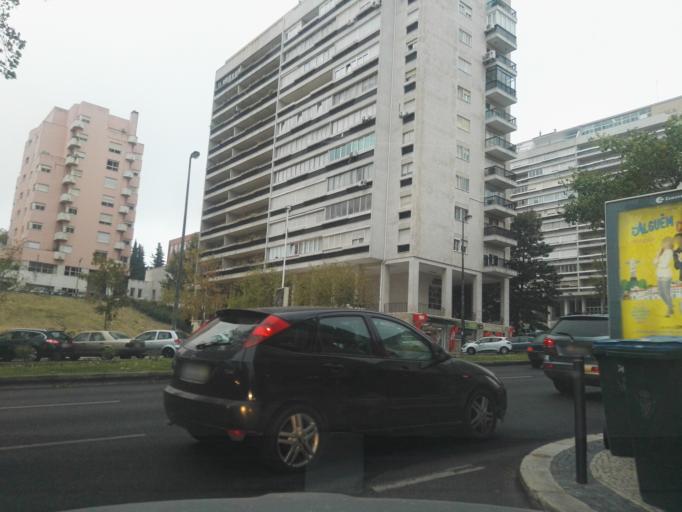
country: PT
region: Lisbon
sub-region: Lisbon
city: Lisbon
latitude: 38.7491
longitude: -9.1346
